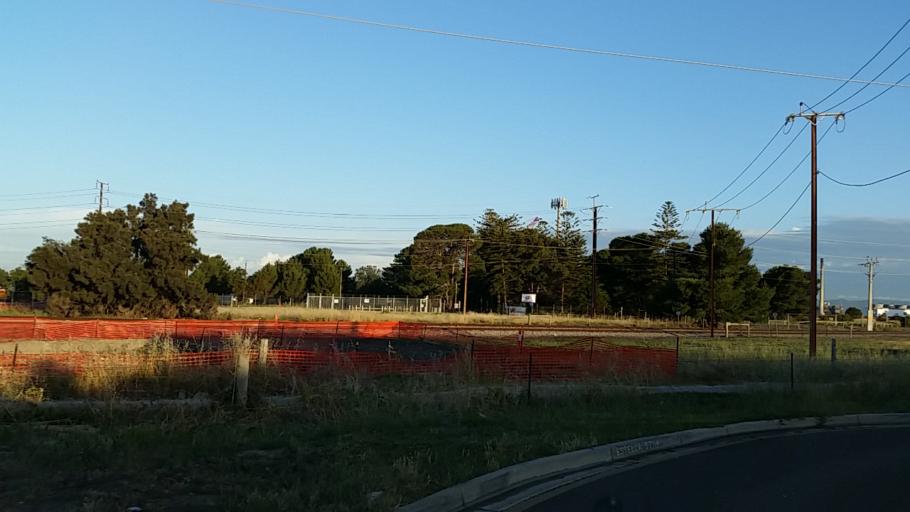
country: AU
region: South Australia
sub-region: Port Adelaide Enfield
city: Birkenhead
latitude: -34.7928
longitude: 138.5037
